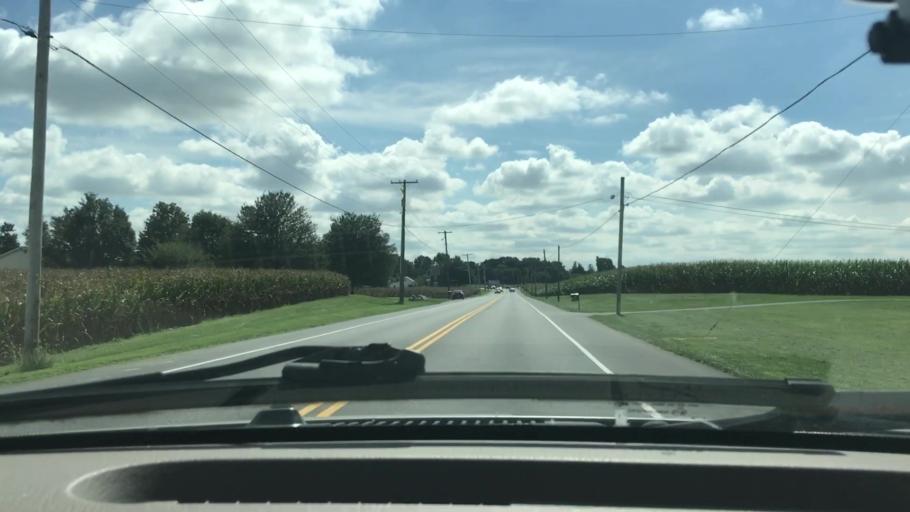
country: US
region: Pennsylvania
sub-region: Lancaster County
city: Manheim
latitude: 40.1298
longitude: -76.3801
